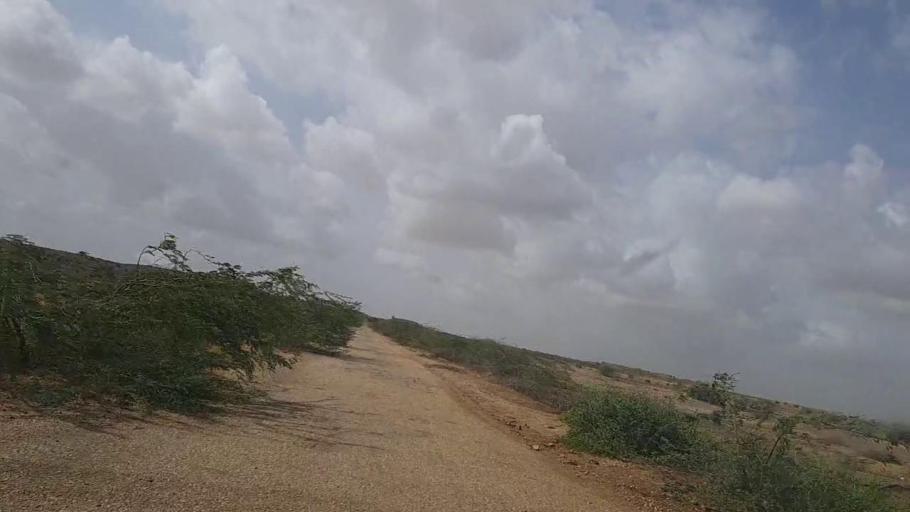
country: PK
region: Sindh
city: Thatta
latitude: 24.8826
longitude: 67.8963
